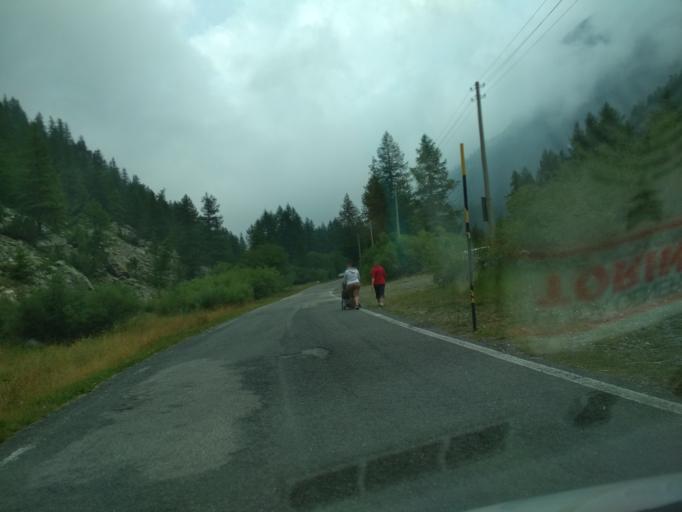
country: IT
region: Piedmont
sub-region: Provincia di Torino
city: Balme
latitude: 45.3055
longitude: 7.1703
